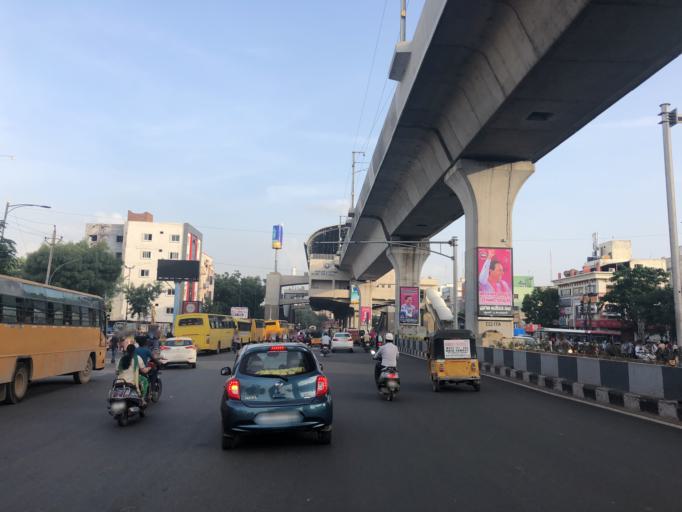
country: IN
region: Telangana
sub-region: Rangareddi
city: Kukatpalli
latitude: 17.4430
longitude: 78.4409
